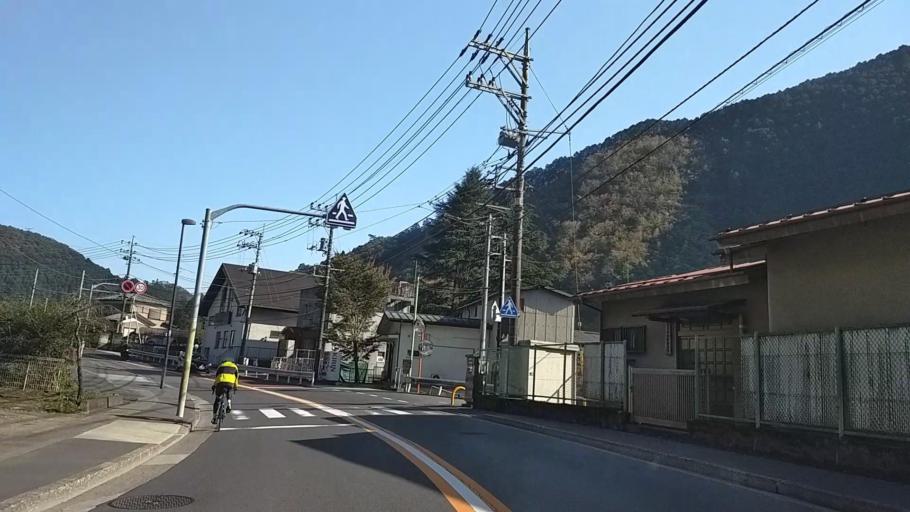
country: JP
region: Tokyo
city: Ome
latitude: 35.8145
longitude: 139.1461
